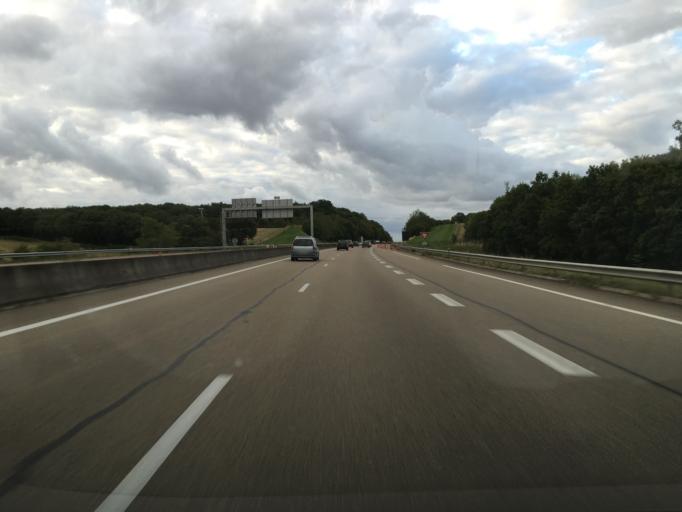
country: FR
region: Bourgogne
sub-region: Departement de l'Yonne
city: Avallon
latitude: 47.5173
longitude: 3.9906
